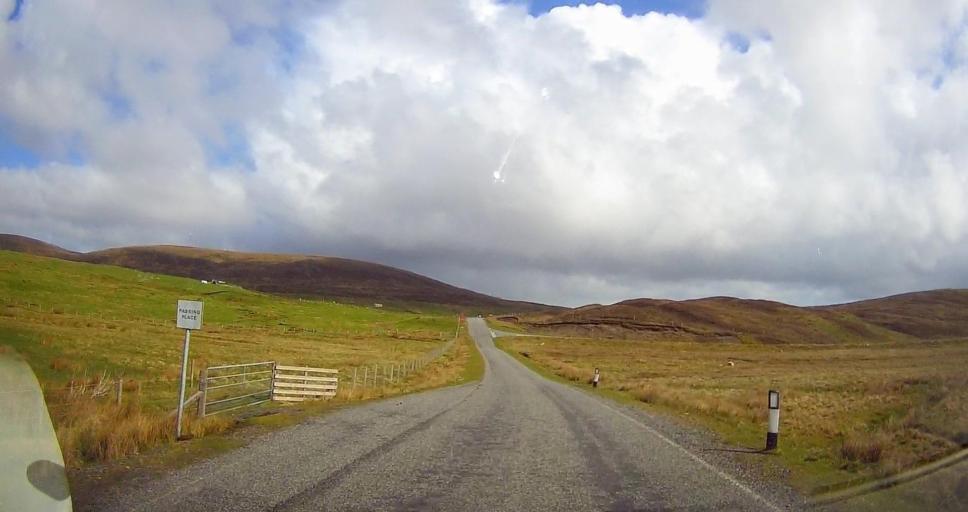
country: GB
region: Scotland
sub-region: Shetland Islands
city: Lerwick
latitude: 60.5169
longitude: -1.3779
